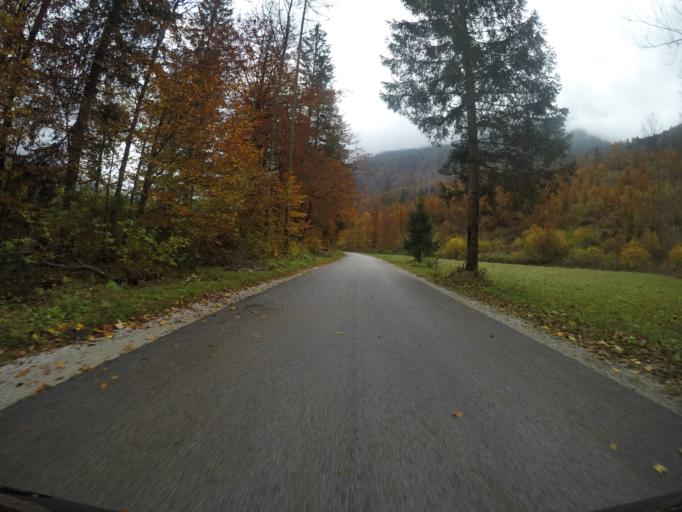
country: SI
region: Jesenice
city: Hrusica
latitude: 46.4238
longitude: 13.9733
